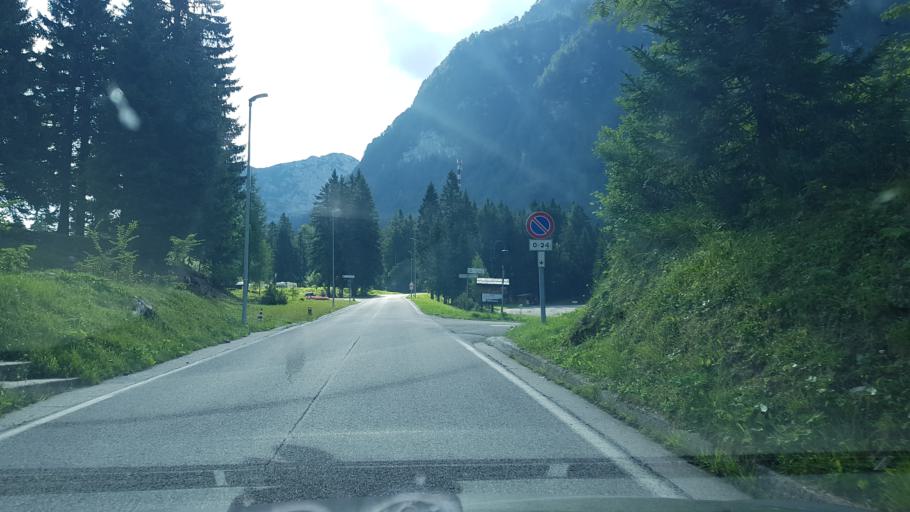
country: SI
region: Bovec
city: Bovec
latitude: 46.3910
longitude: 13.4739
